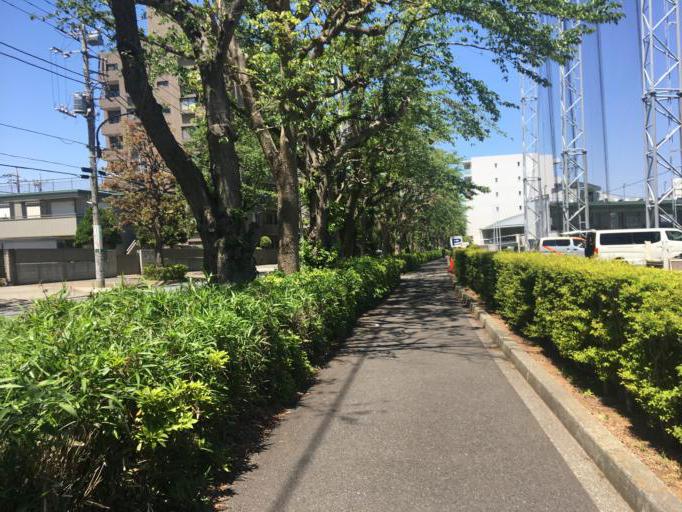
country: JP
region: Saitama
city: Wako
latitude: 35.7652
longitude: 139.6358
